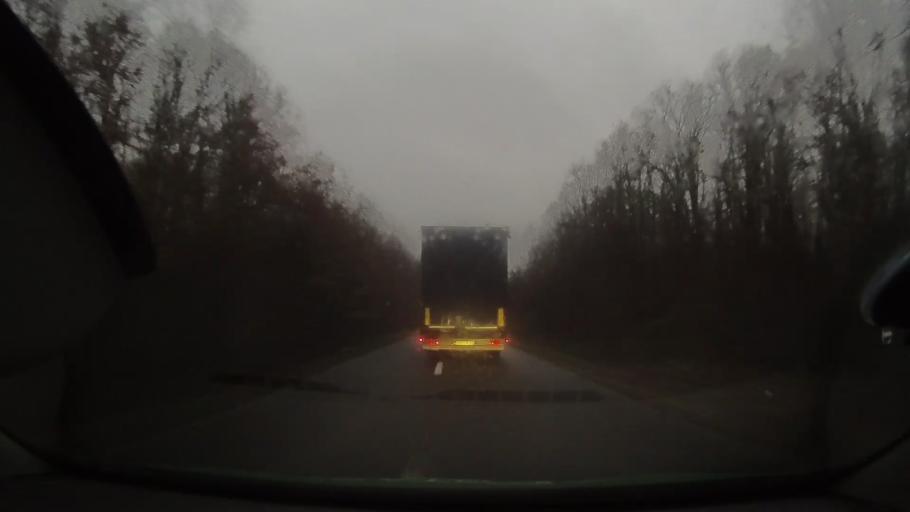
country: RO
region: Arad
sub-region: Comuna Beliu
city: Beliu
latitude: 46.5057
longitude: 21.9708
